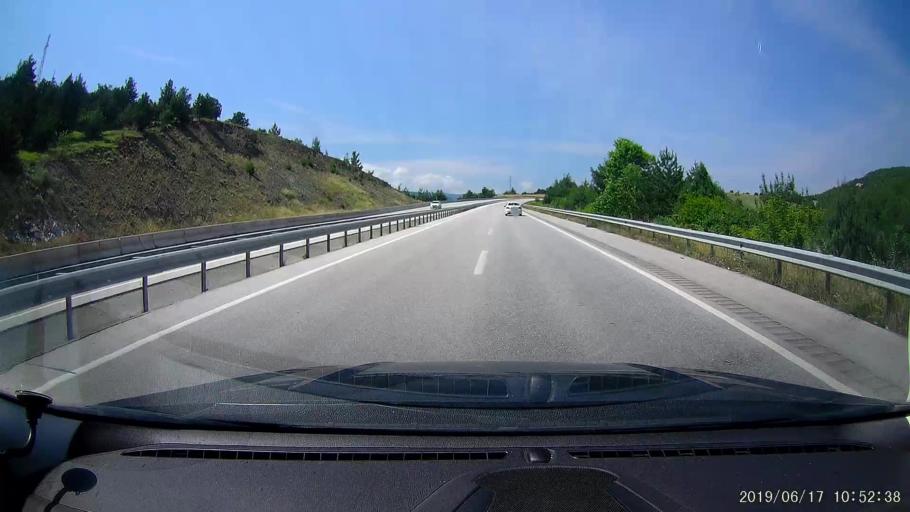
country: TR
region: Corum
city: Hacihamza
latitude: 41.0860
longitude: 34.3389
